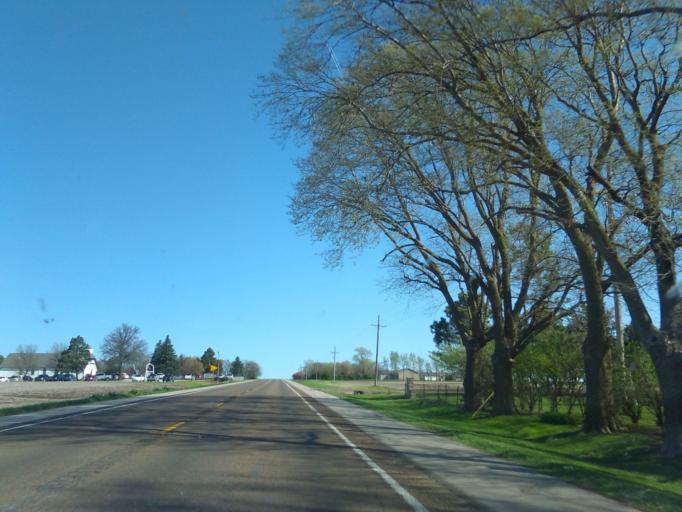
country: US
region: Nebraska
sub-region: Dodge County
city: Fremont
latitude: 41.3443
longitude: -96.5022
